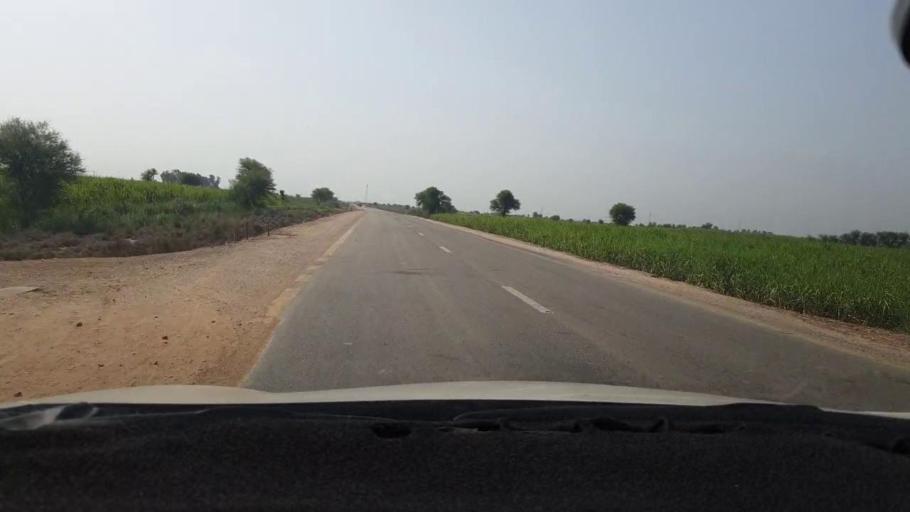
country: PK
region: Sindh
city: Jhol
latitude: 25.8442
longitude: 69.0616
